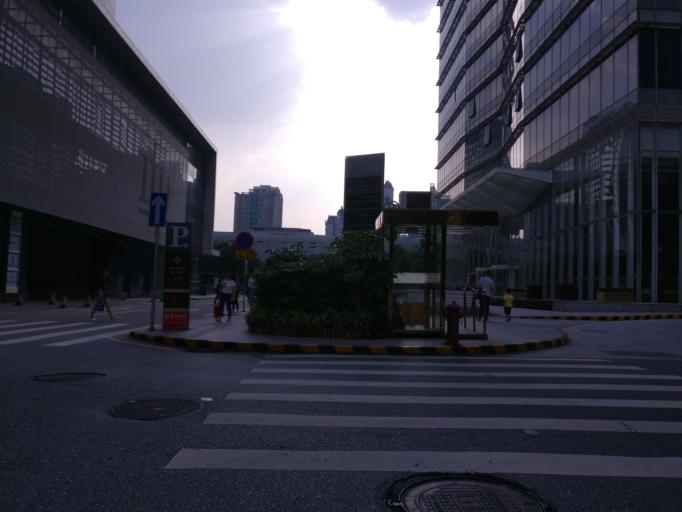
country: CN
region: Guangdong
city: Wushan
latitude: 23.1196
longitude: 113.3171
